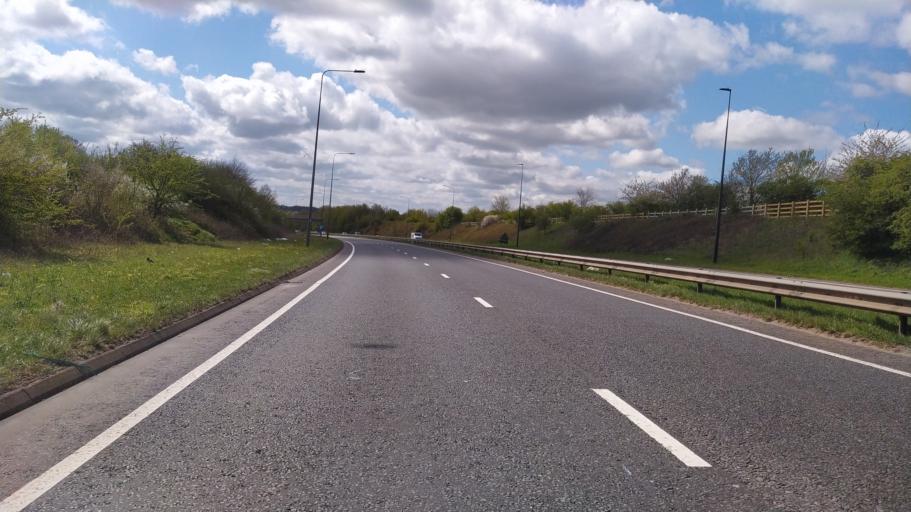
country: GB
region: England
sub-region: South Gloucestershire
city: Kingswood
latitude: 51.4402
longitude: -2.5093
